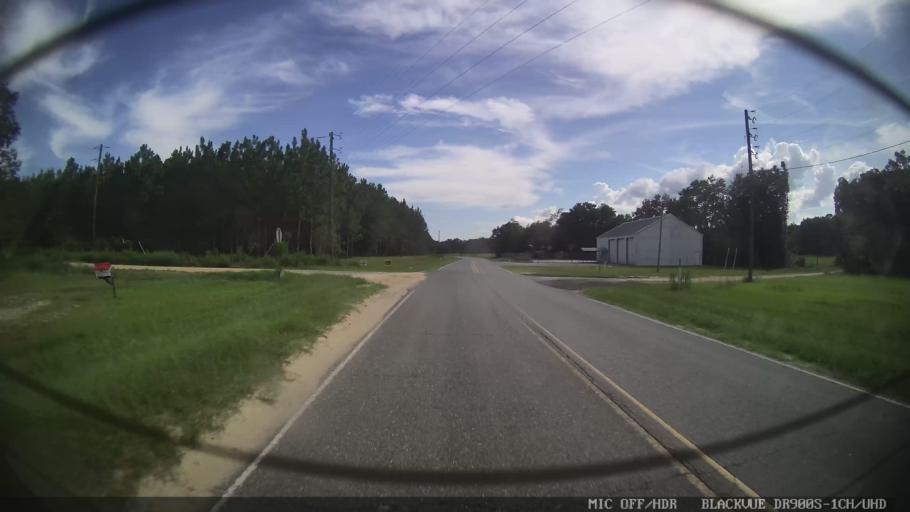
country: US
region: Georgia
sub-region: Echols County
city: Statenville
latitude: 30.6016
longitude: -83.2228
